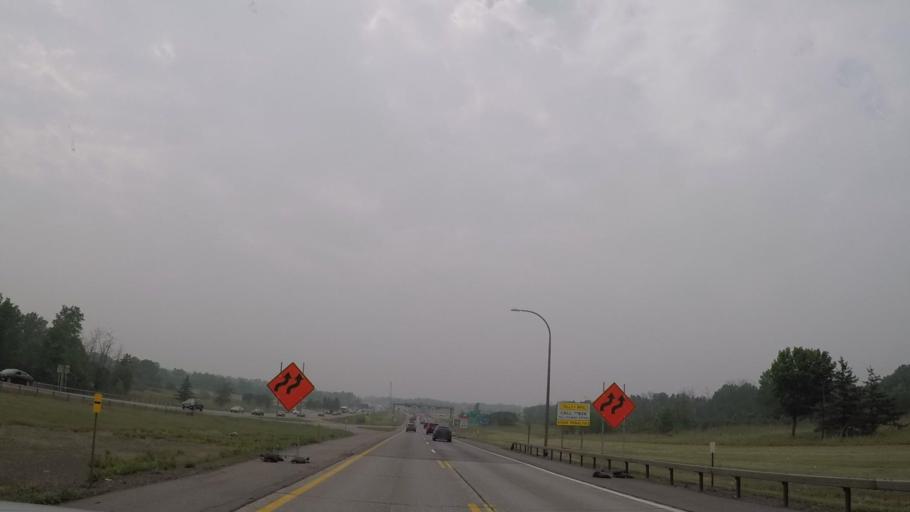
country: US
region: New York
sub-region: Erie County
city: Grandyle Village
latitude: 43.0014
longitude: -78.9414
